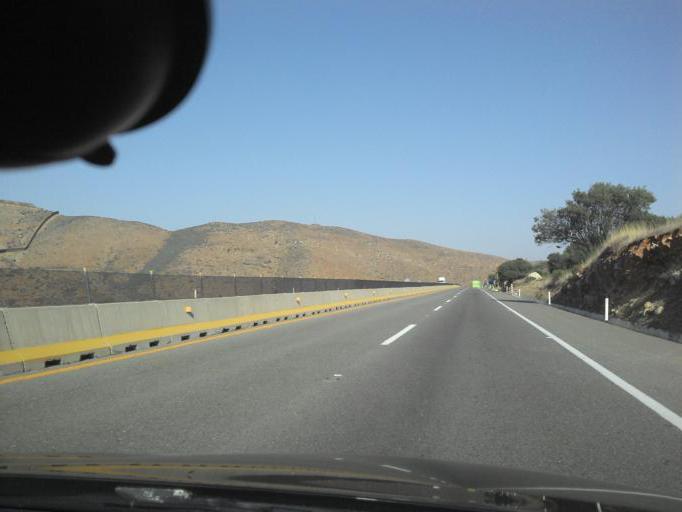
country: MX
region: Baja California
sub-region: Tijuana
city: El Nino
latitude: 32.5581
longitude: -116.8129
